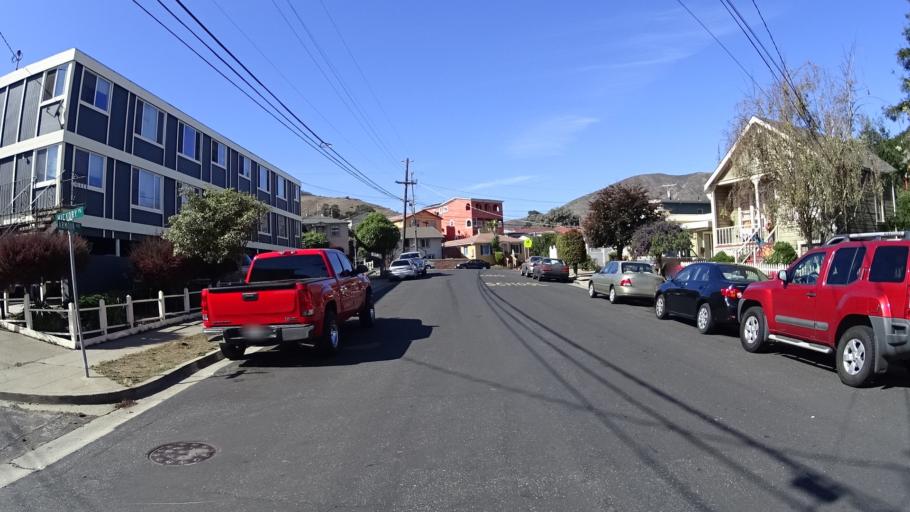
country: US
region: California
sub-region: San Mateo County
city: South San Francisco
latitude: 37.6619
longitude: -122.4084
